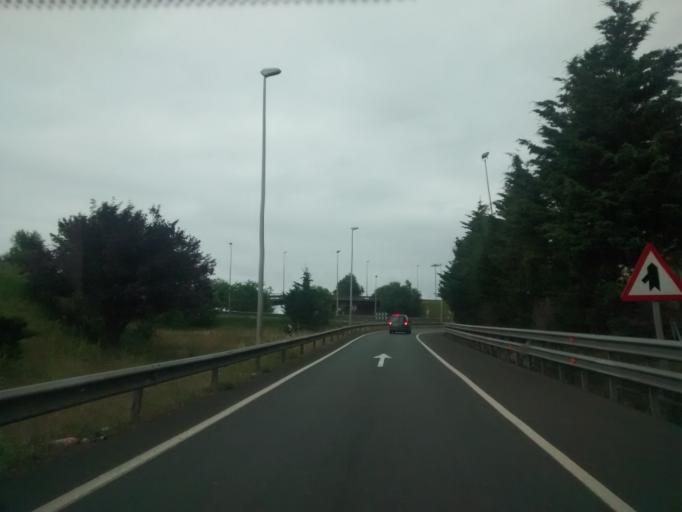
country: ES
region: Cantabria
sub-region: Provincia de Cantabria
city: Santander
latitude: 43.4398
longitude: -3.8358
